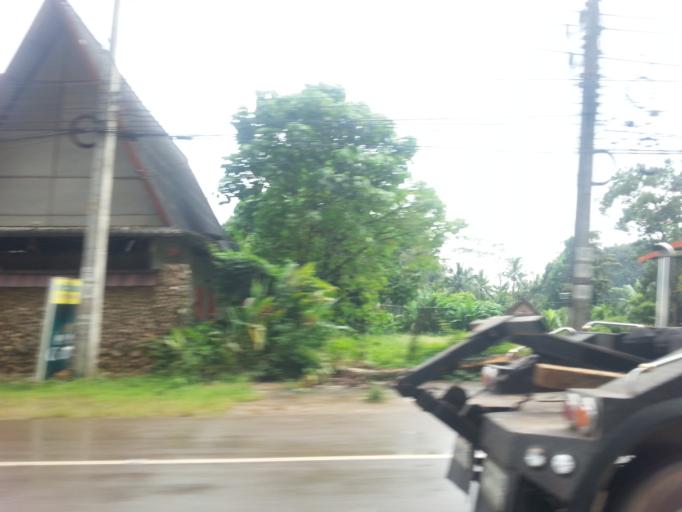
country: TH
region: Krabi
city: Krabi
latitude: 8.0863
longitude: 98.8780
